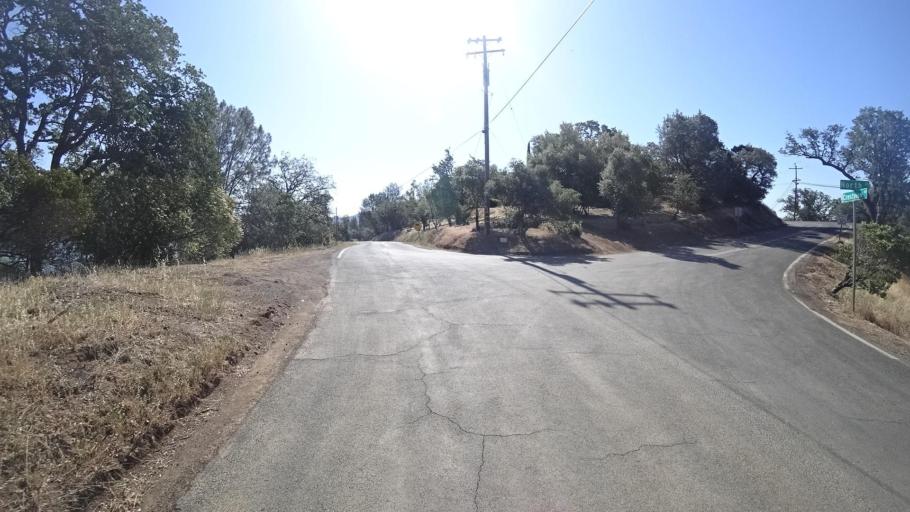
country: US
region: California
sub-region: Lake County
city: Clearlake Oaks
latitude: 39.0042
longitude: -122.7156
